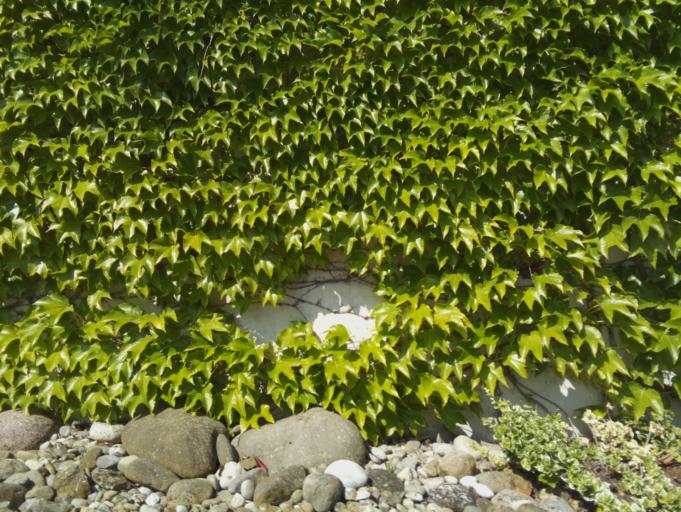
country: CH
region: Zurich
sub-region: Bezirk Andelfingen
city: Grossandelfingen
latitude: 47.5925
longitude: 8.6785
